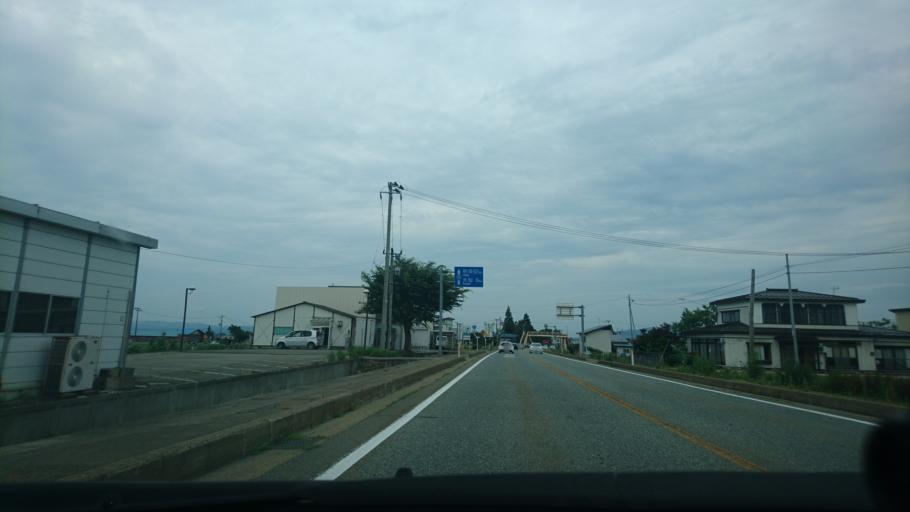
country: JP
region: Akita
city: Omagari
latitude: 39.4154
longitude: 140.5484
